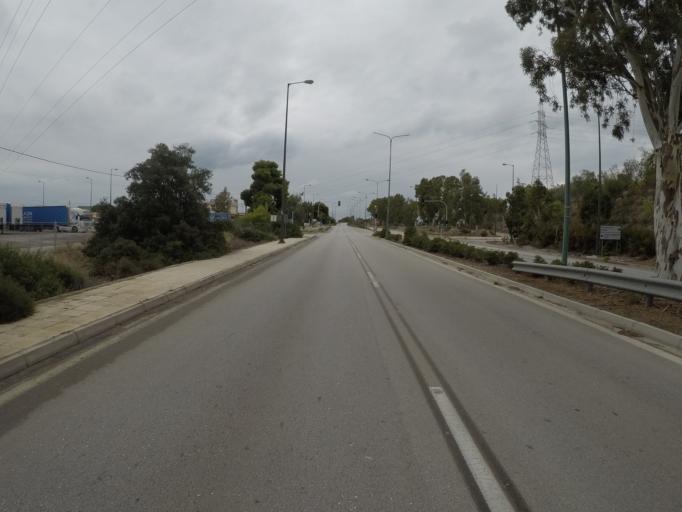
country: GR
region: Peloponnese
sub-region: Nomos Korinthias
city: Kyras Vrysi
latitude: 37.9329
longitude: 22.9908
